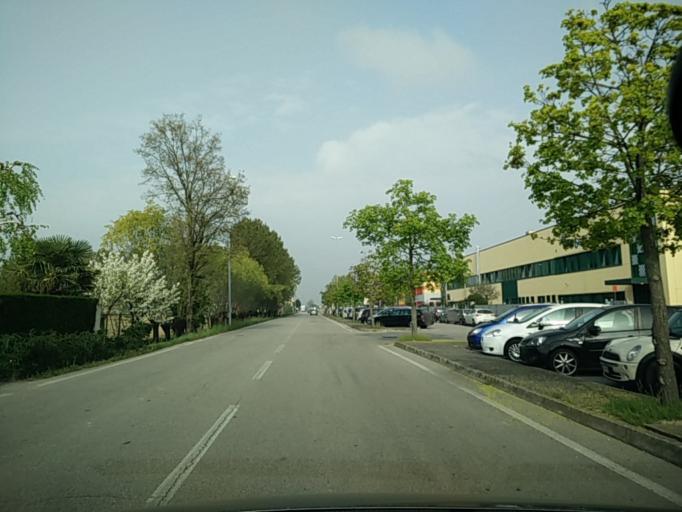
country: IT
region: Veneto
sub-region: Provincia di Venezia
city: Caselle
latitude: 45.5018
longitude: 12.0148
